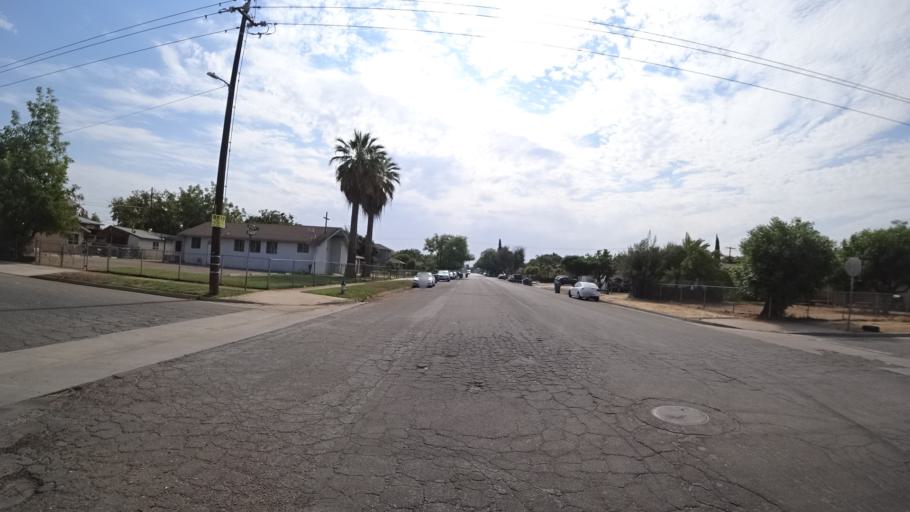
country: US
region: California
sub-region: Fresno County
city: Fresno
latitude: 36.7318
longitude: -119.8101
